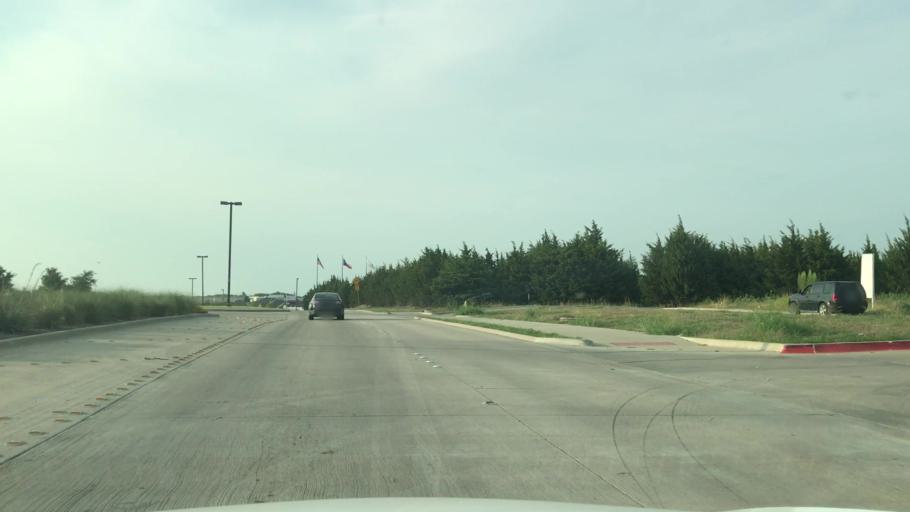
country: US
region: Texas
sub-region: Rockwall County
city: Rockwall
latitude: 32.9075
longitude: -96.4310
